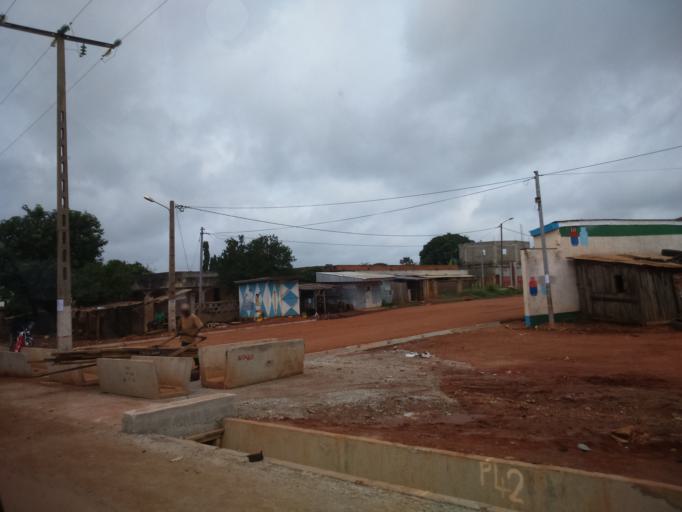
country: CI
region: Moyen-Comoe
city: Abengourou
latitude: 6.7257
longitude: -3.5045
